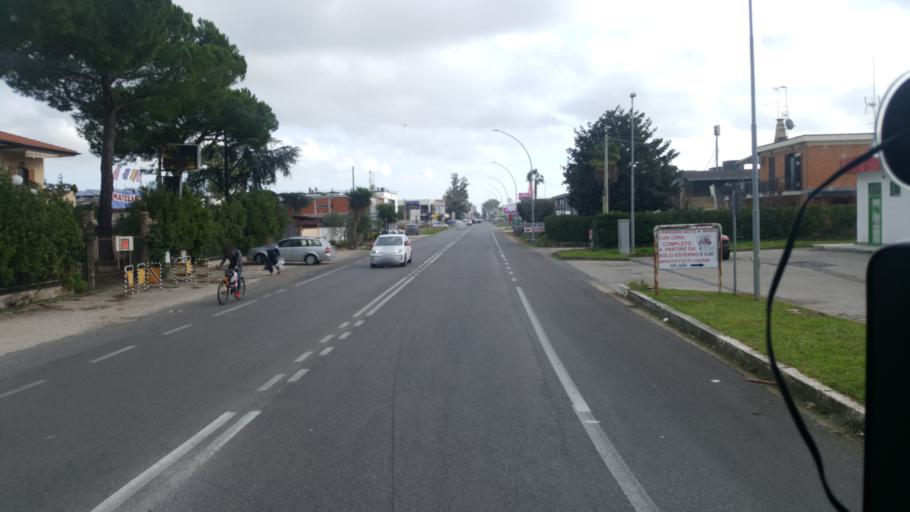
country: IT
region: Latium
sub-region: Provincia di Latina
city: Latina
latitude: 41.4776
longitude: 12.8755
